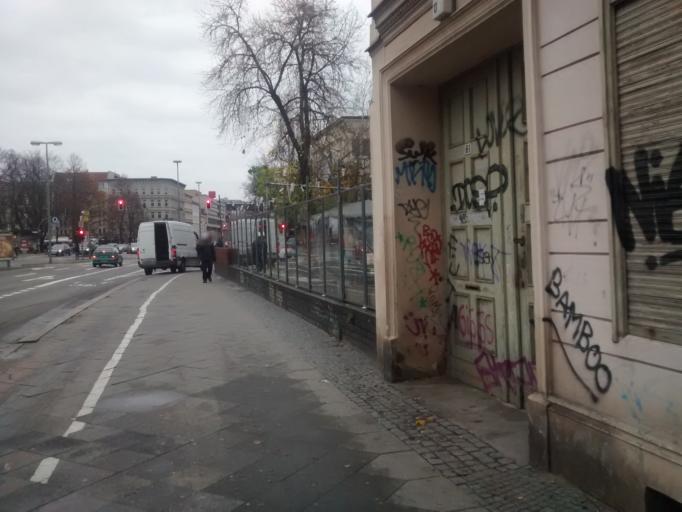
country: DE
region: Berlin
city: Moabit
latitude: 52.5271
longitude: 13.3431
